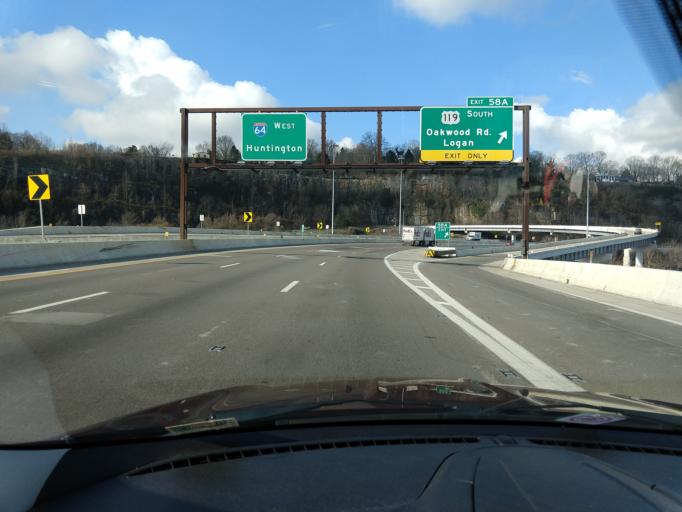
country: US
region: West Virginia
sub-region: Kanawha County
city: Charleston
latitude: 38.3569
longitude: -81.6494
